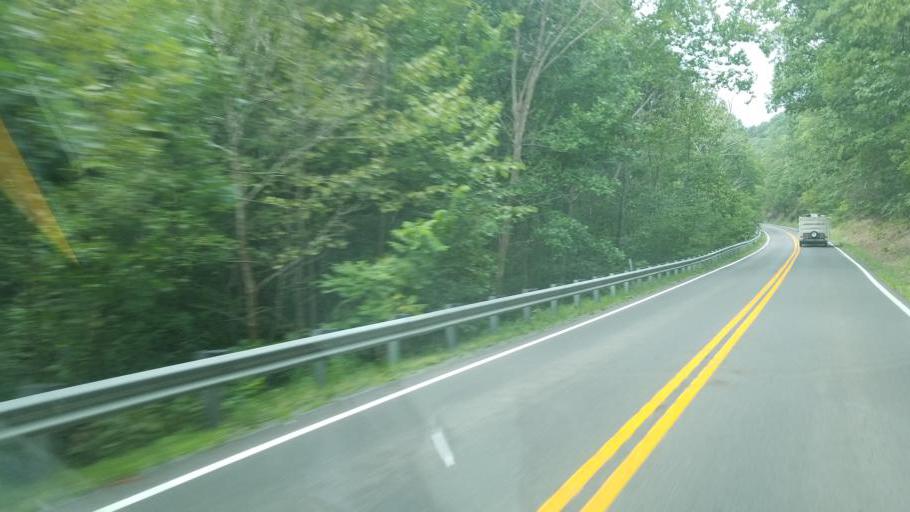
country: US
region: West Virginia
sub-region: Mineral County
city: Fort Ashby
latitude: 39.5413
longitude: -78.5030
